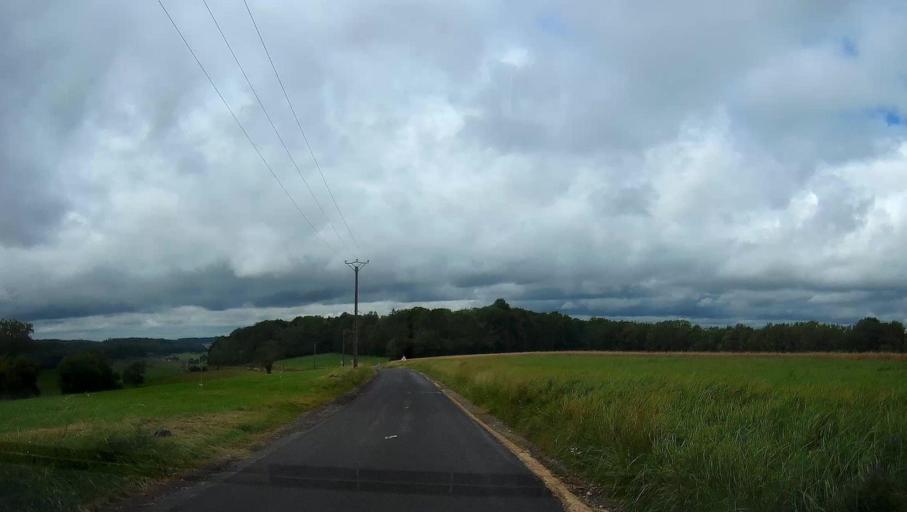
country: FR
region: Champagne-Ardenne
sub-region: Departement des Ardennes
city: Rimogne
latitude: 49.7641
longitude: 4.5029
